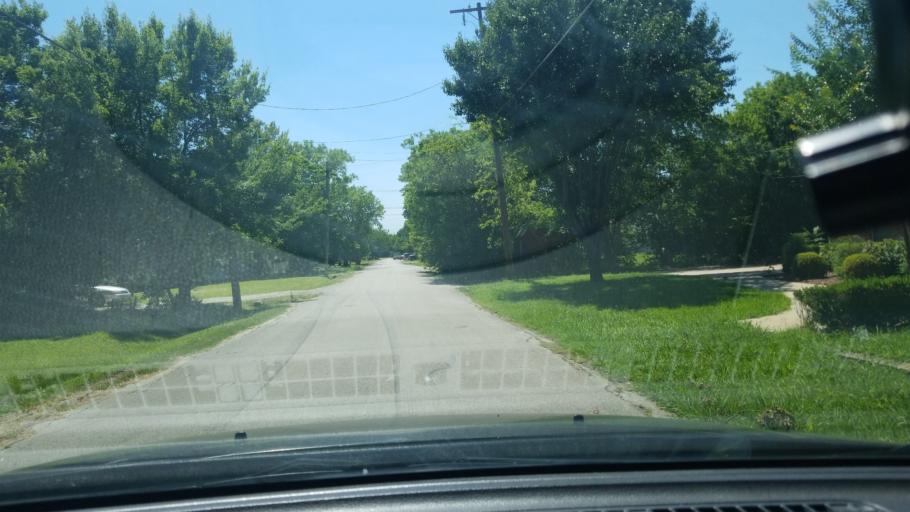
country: US
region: Texas
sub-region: Dallas County
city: Mesquite
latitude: 32.7654
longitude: -96.6048
